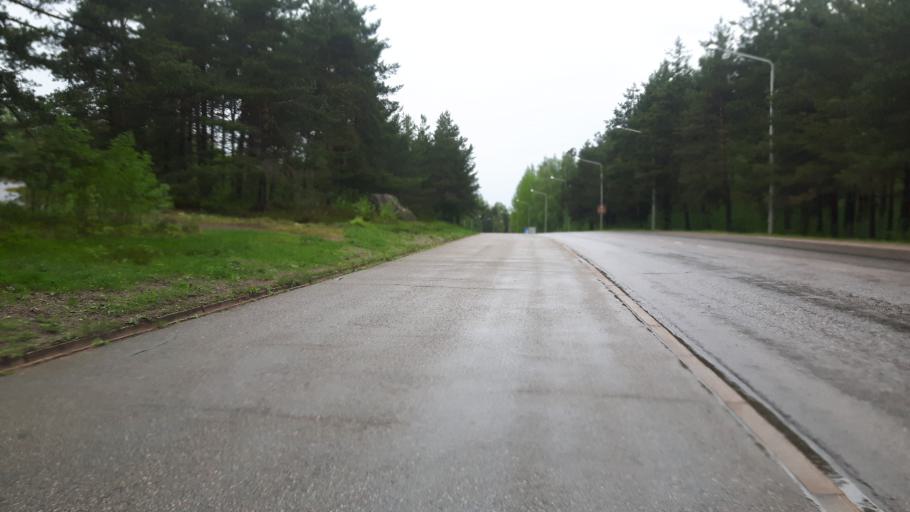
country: FI
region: Kymenlaakso
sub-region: Kotka-Hamina
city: Kotka
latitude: 60.4908
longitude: 26.9022
